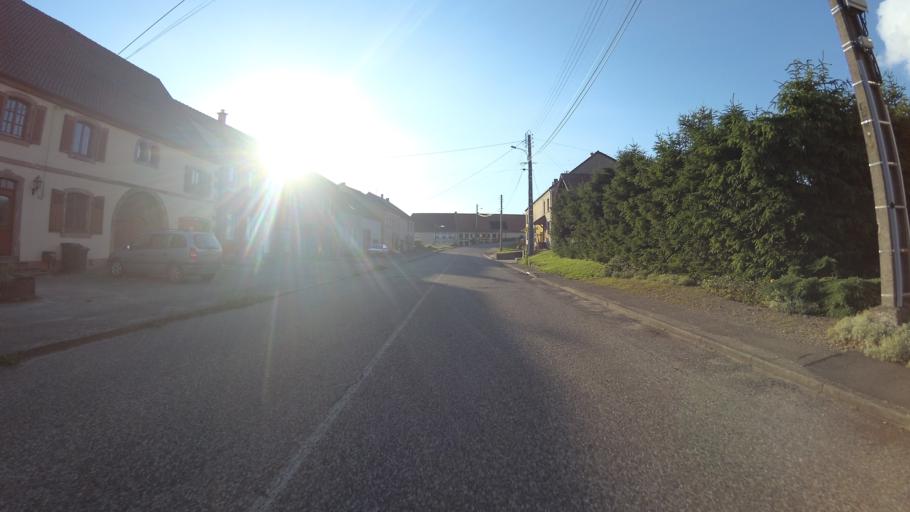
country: FR
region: Alsace
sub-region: Departement du Bas-Rhin
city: Herbitzheim
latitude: 49.0189
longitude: 7.0768
